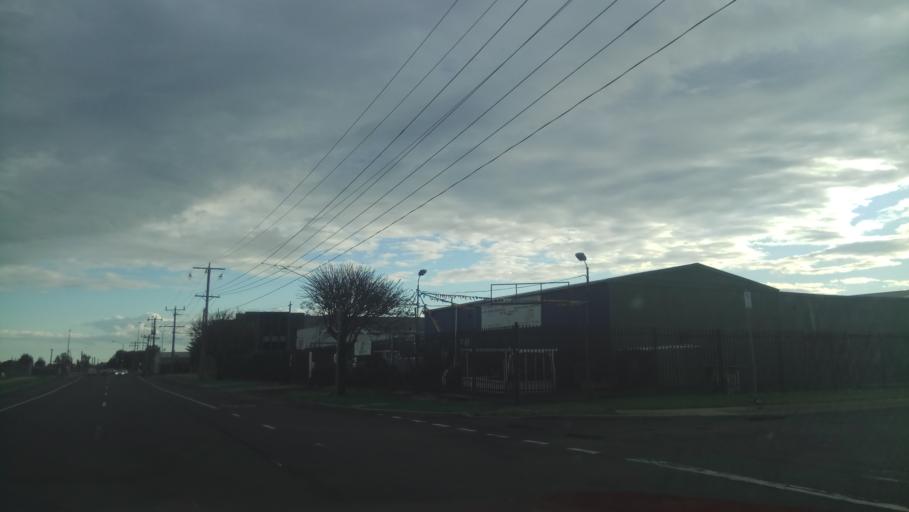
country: AU
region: Victoria
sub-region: Hobsons Bay
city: Williamstown North
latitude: -37.8534
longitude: 144.8677
